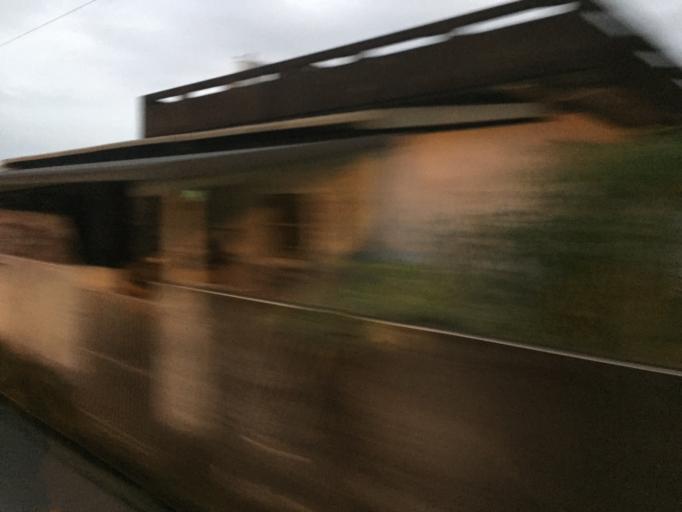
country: TW
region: Taiwan
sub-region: Yilan
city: Yilan
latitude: 24.7733
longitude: 121.7462
